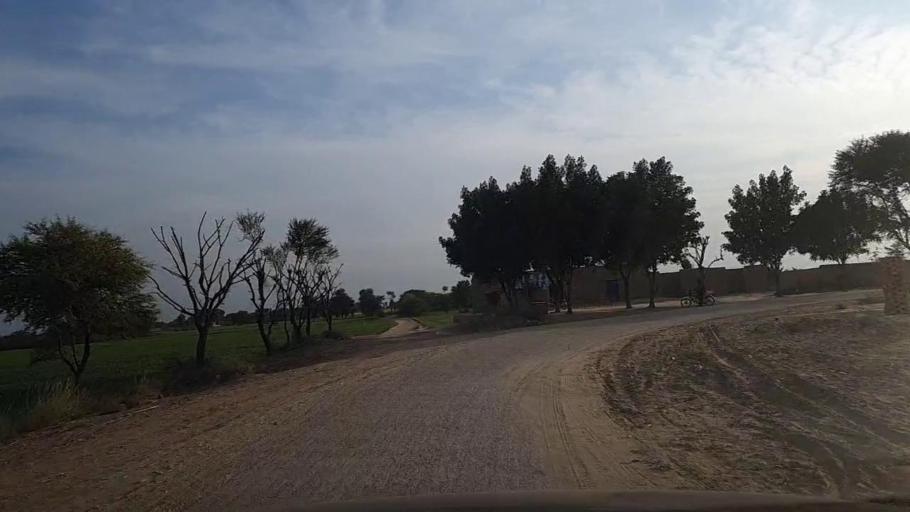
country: PK
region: Sindh
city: Jam Sahib
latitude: 26.4322
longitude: 68.5715
